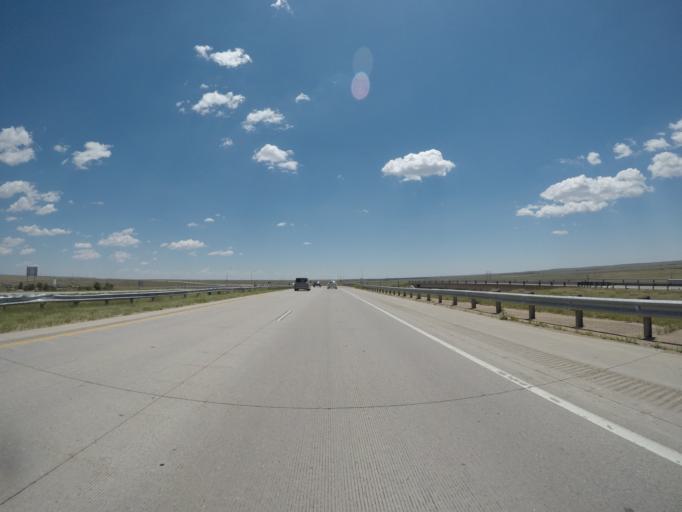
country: US
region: Colorado
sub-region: Lincoln County
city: Limon
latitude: 39.2640
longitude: -103.6674
